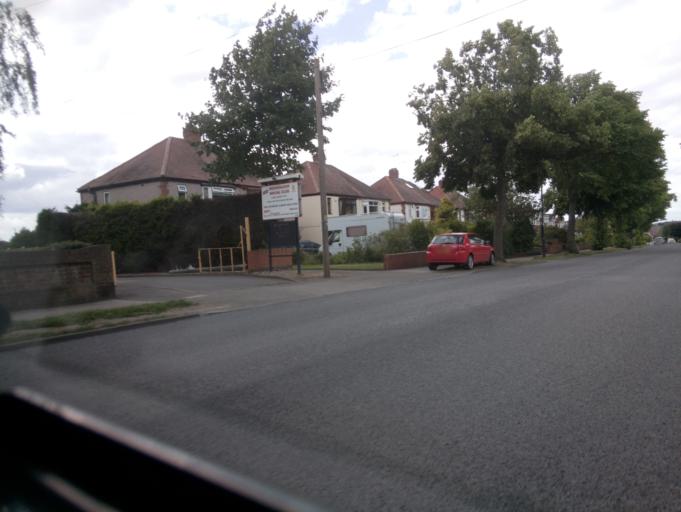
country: GB
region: England
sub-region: Warwickshire
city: Nuneaton
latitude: 52.5361
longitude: -1.4656
